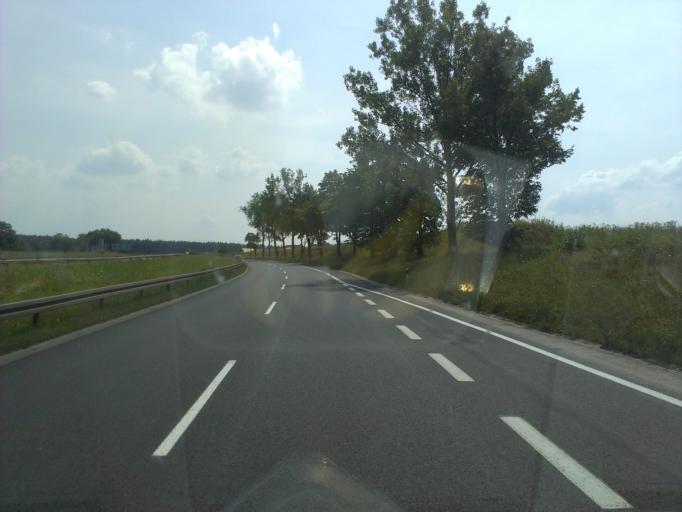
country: PL
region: Lower Silesian Voivodeship
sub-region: Powiat lubinski
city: Lubin
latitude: 51.3880
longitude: 16.2200
